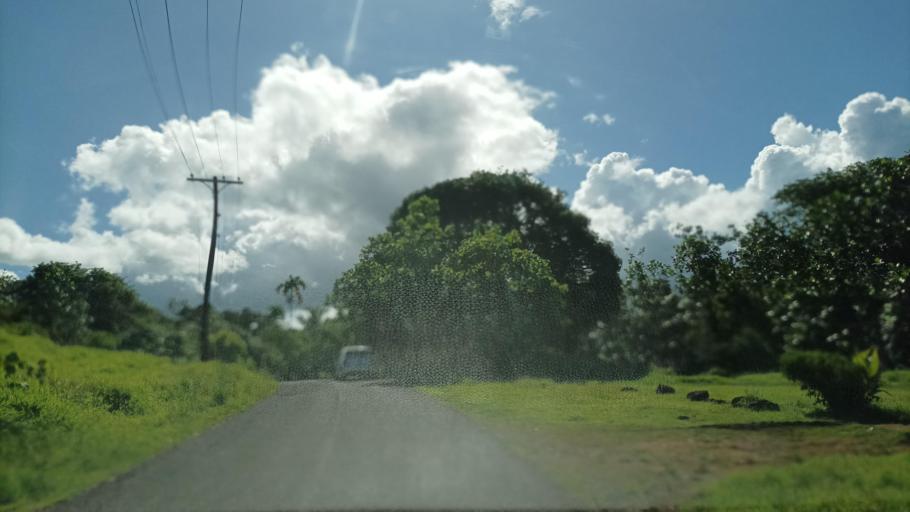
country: FM
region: Pohnpei
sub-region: Madolenihm Municipality
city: Madolenihm Municipality Government
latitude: 6.8427
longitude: 158.3077
